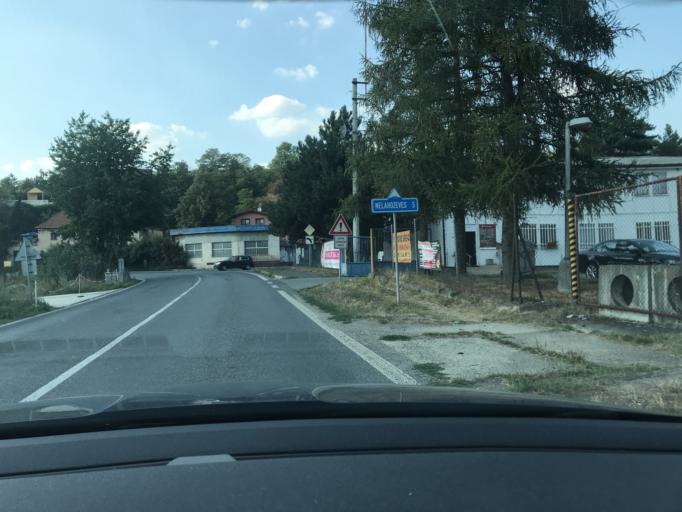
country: CZ
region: Central Bohemia
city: Kralupy nad Vltavou
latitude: 50.2320
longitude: 14.2801
